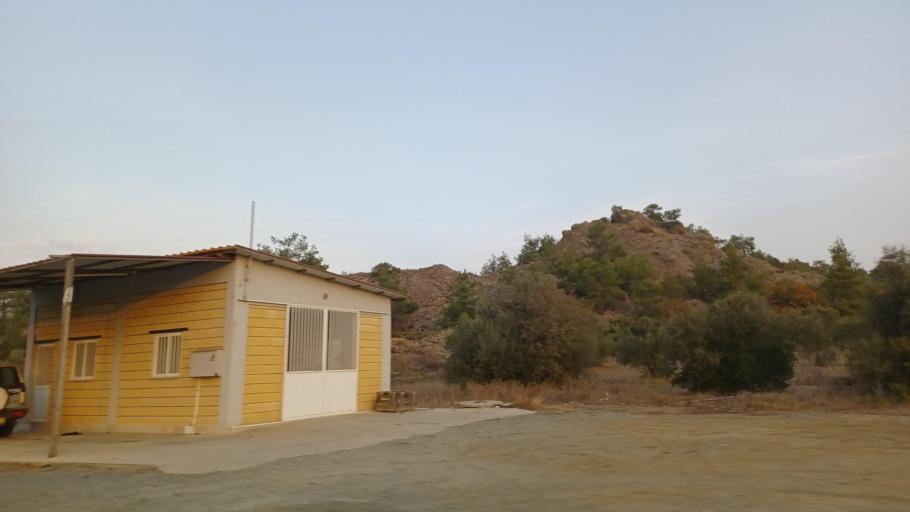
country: CY
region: Larnaka
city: Kornos
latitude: 34.9144
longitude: 33.3716
